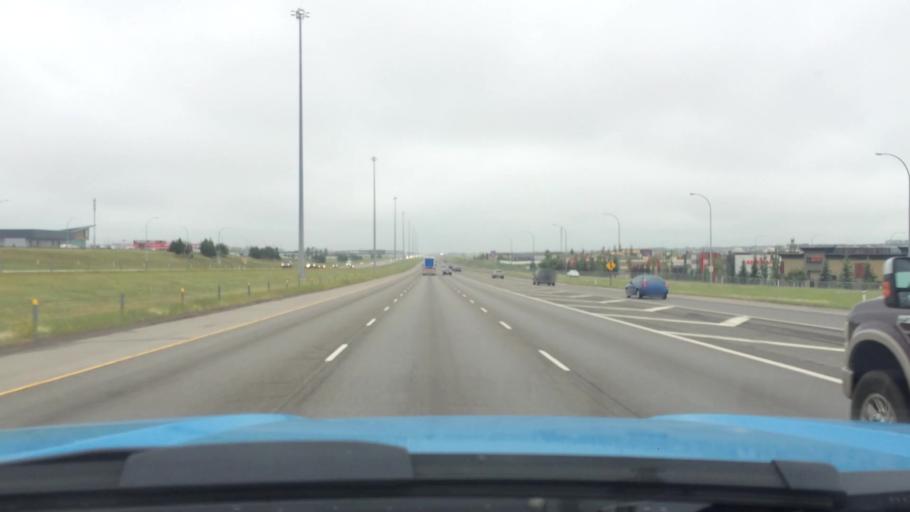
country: CA
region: Alberta
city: Airdrie
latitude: 51.2695
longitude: -114.0017
